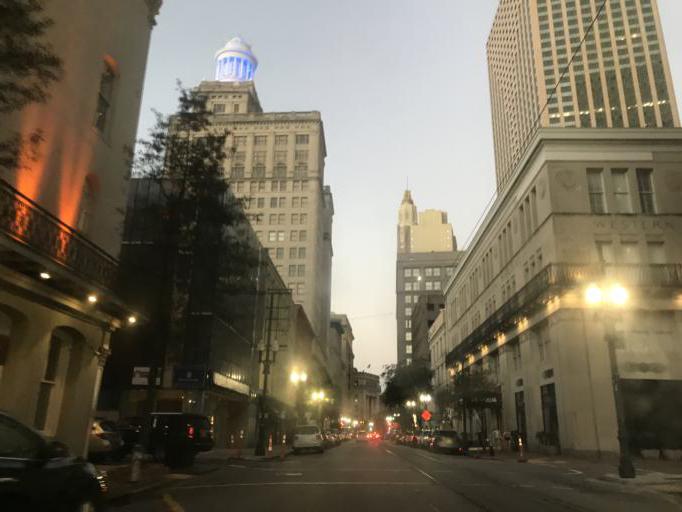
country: US
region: Louisiana
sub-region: Orleans Parish
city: New Orleans
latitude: 29.9505
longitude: -90.0716
